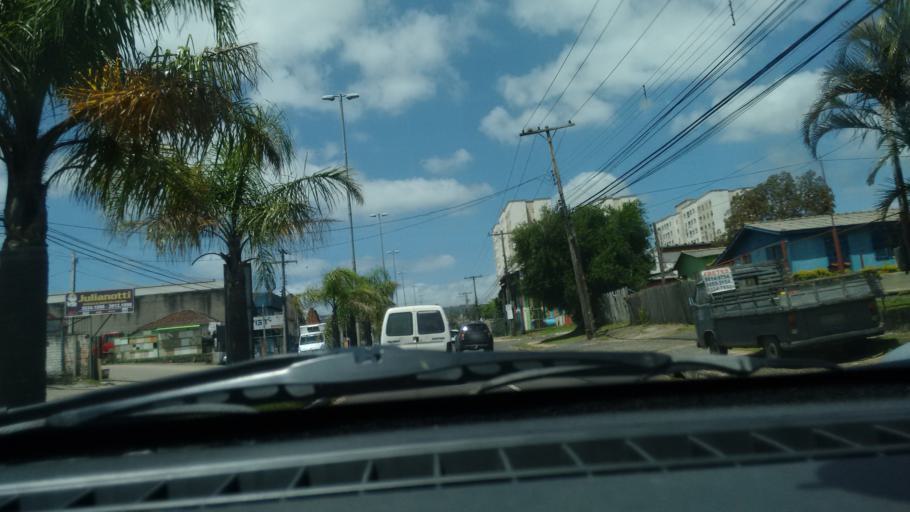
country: BR
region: Rio Grande do Sul
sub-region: Cachoeirinha
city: Cachoeirinha
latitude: -30.0175
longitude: -51.1194
